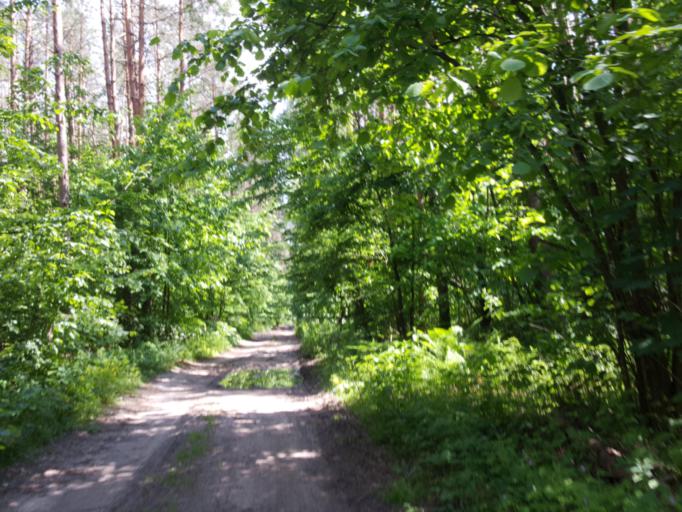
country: PL
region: Podlasie
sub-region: Powiat hajnowski
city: Hajnowka
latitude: 52.5819
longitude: 23.6169
